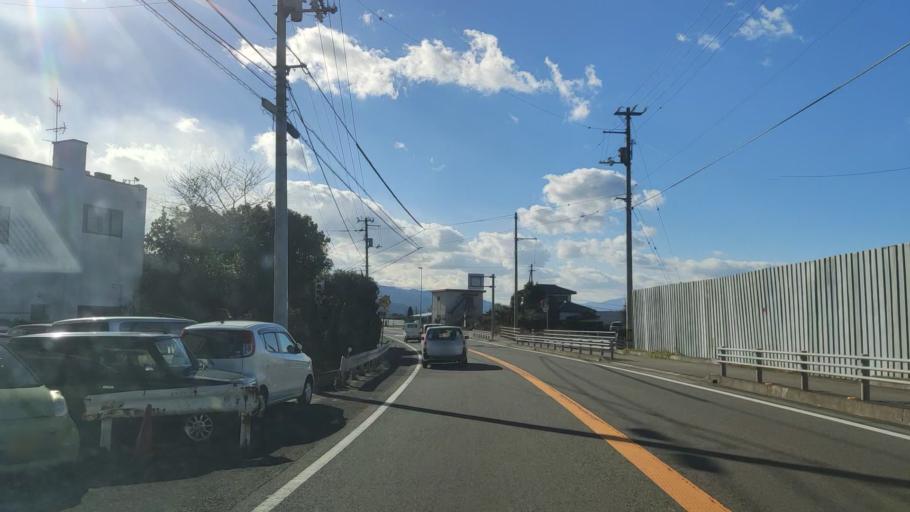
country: JP
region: Ehime
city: Saijo
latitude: 33.9174
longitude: 133.2198
